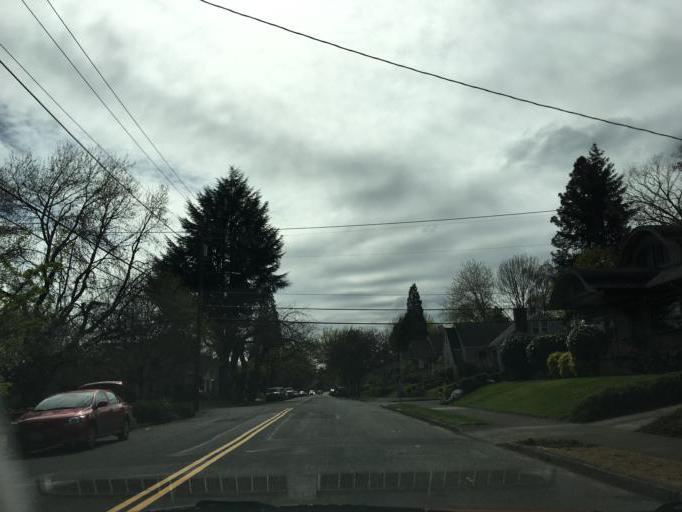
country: US
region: Oregon
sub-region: Clackamas County
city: Milwaukie
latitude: 45.4706
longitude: -122.6473
